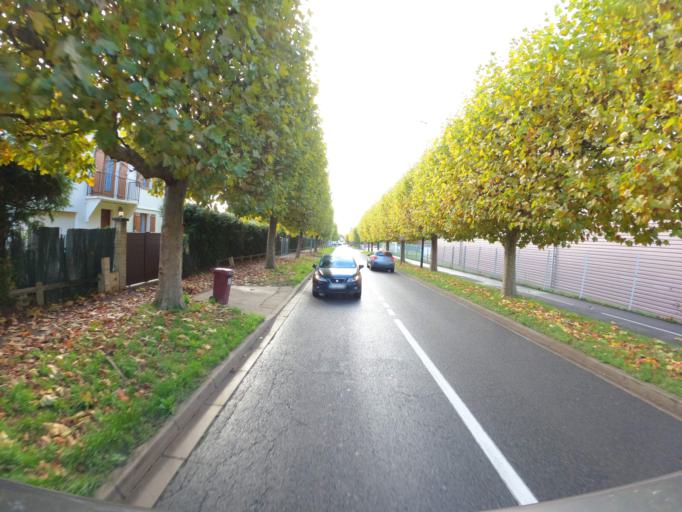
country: FR
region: Ile-de-France
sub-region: Departement de Seine-et-Marne
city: Brou-sur-Chantereine
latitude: 48.8884
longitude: 2.6206
